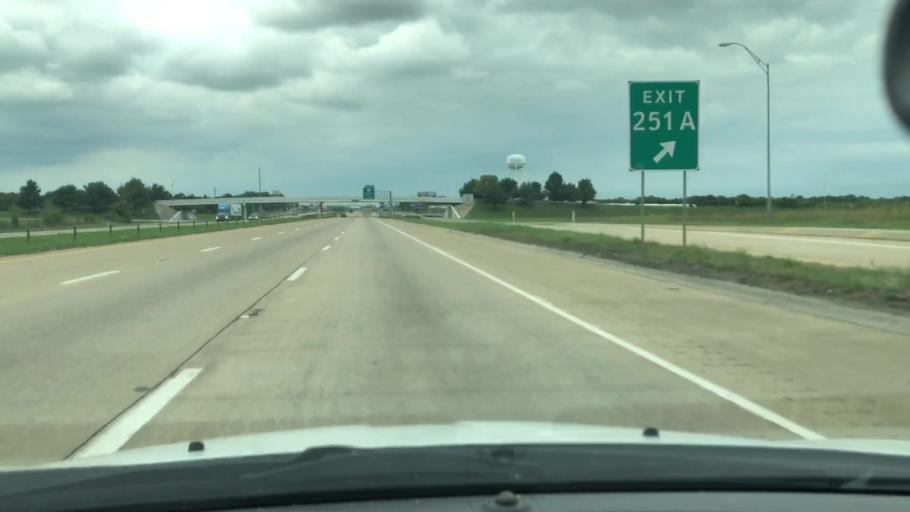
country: US
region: Texas
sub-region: Ellis County
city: Ennis
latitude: 32.3227
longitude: -96.6073
